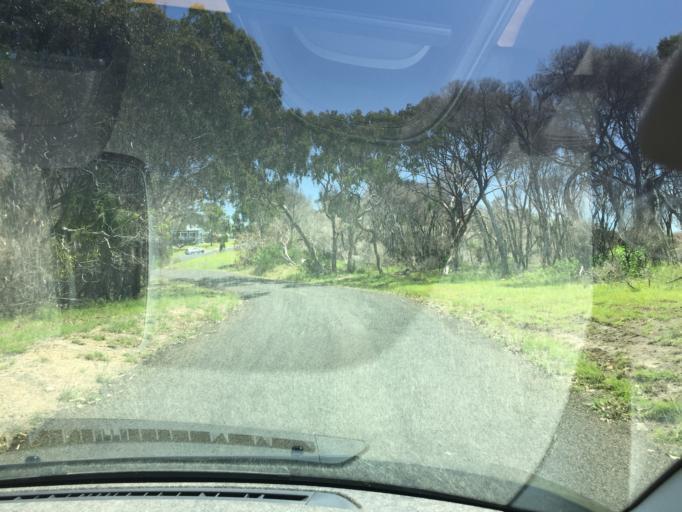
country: AU
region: New South Wales
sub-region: Bega Valley
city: Bega
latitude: -36.7367
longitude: 149.9844
